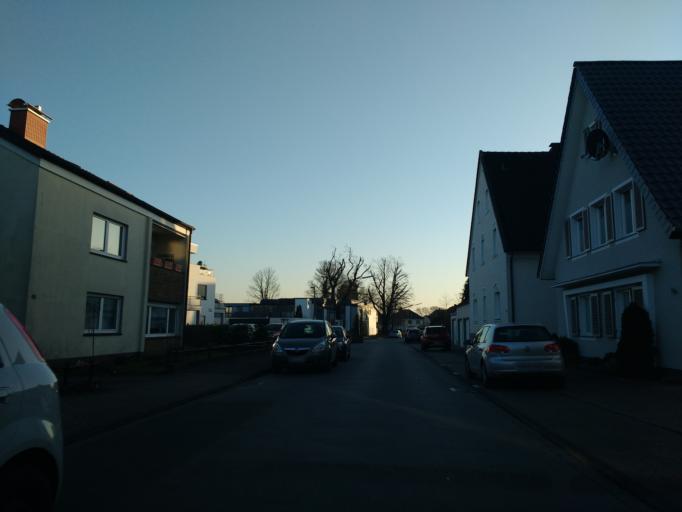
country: DE
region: North Rhine-Westphalia
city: Bad Lippspringe
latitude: 51.7784
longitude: 8.8129
